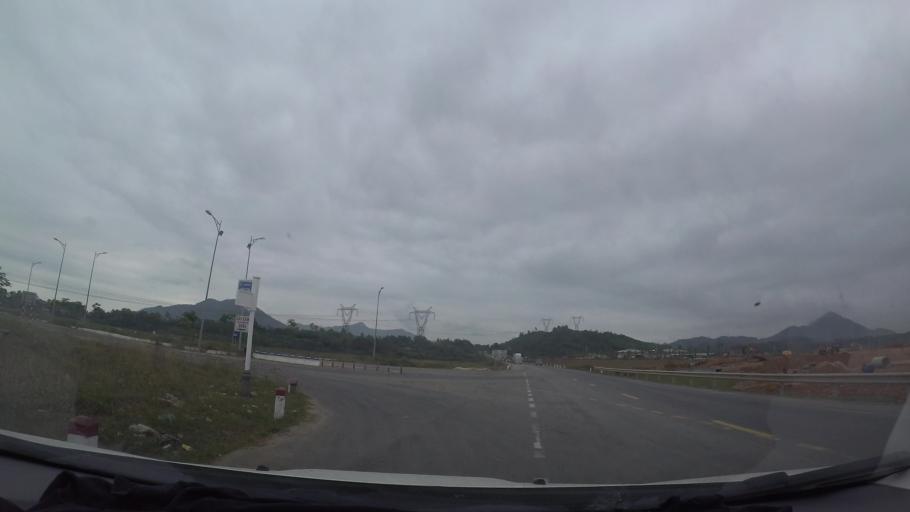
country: VN
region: Da Nang
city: Lien Chieu
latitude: 16.0748
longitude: 108.0882
